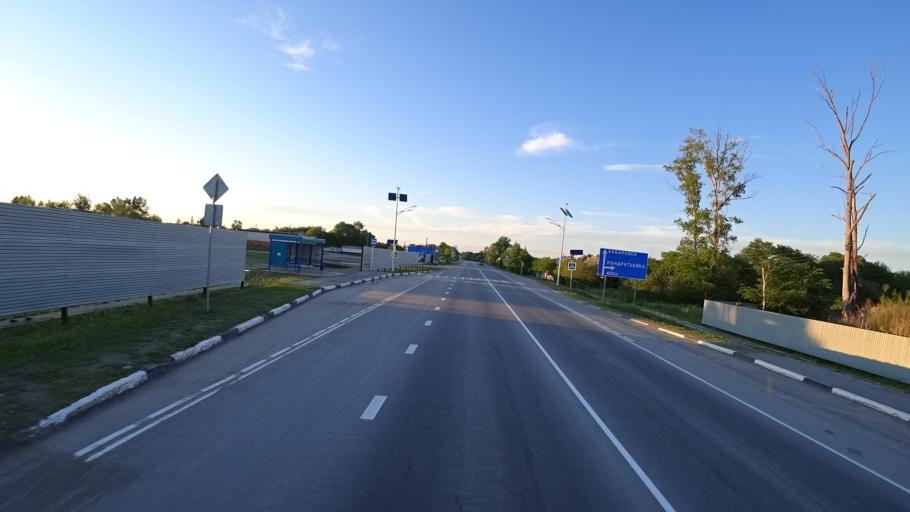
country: RU
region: Khabarovsk Krai
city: Khor
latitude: 47.8523
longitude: 134.9608
